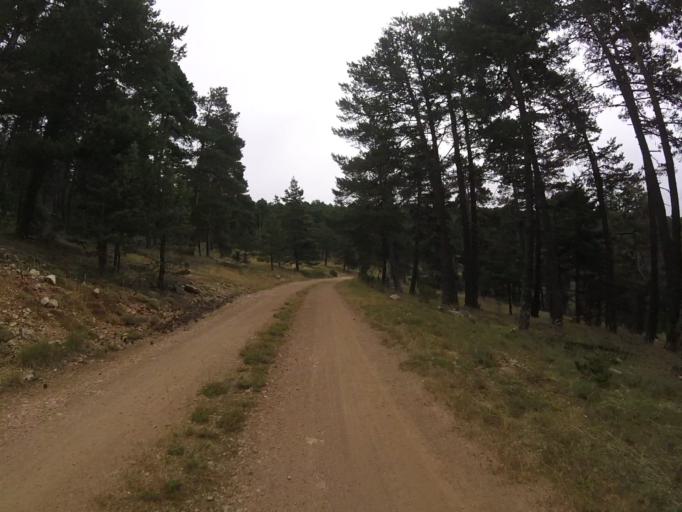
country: ES
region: Aragon
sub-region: Provincia de Teruel
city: Valdelinares
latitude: 40.3608
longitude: -0.6066
